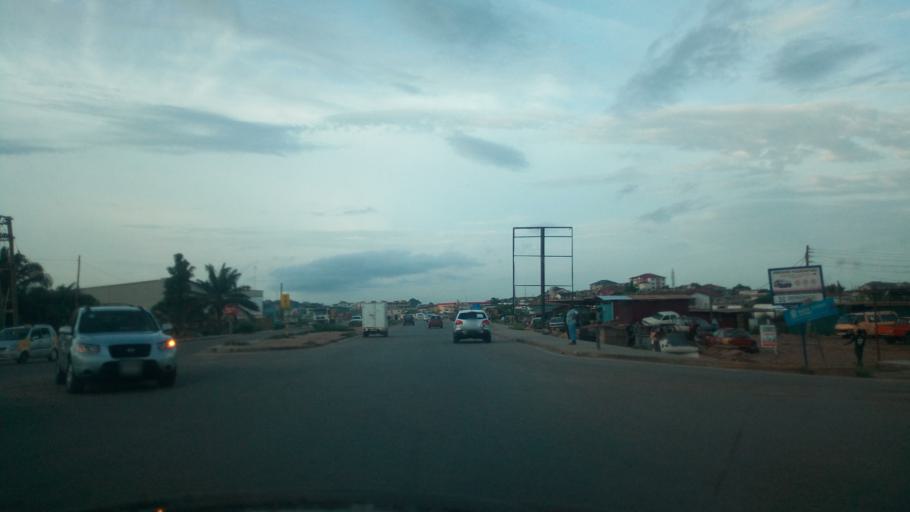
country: GH
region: Western
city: Takoradi
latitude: 4.9216
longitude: -1.7857
